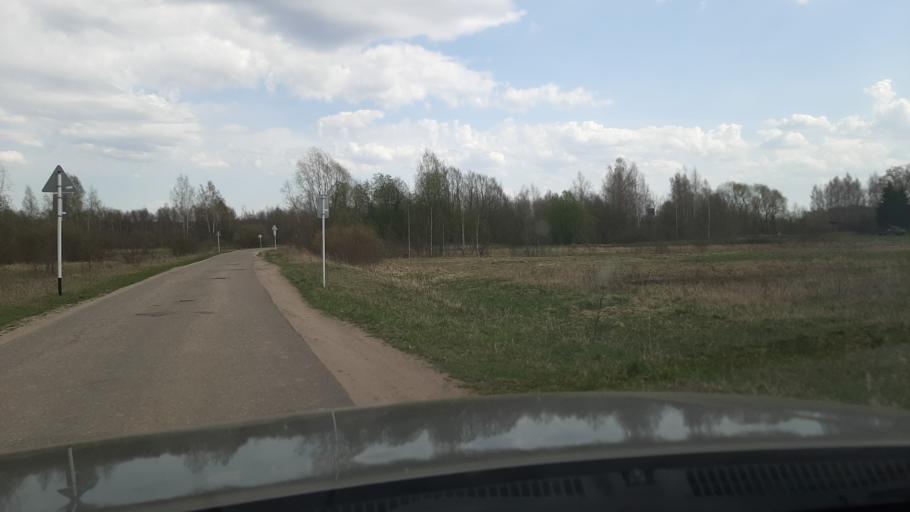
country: RU
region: Ivanovo
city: Furmanov
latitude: 57.3021
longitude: 41.1634
